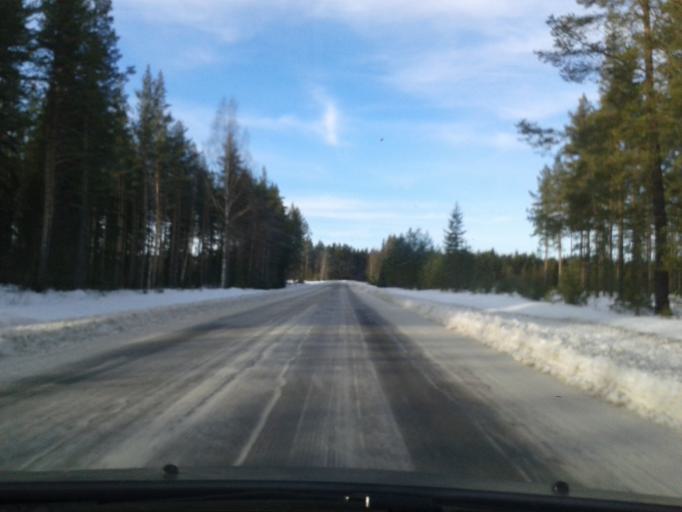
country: SE
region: Vaesternorrland
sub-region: OErnskoeldsviks Kommun
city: Bredbyn
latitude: 63.5410
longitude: 17.9589
